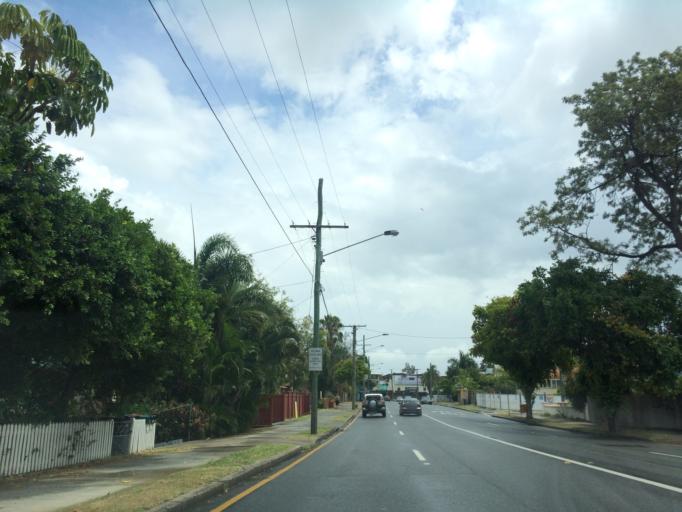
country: AU
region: Queensland
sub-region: Brisbane
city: Woolloongabba
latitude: -27.4780
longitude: 153.0482
